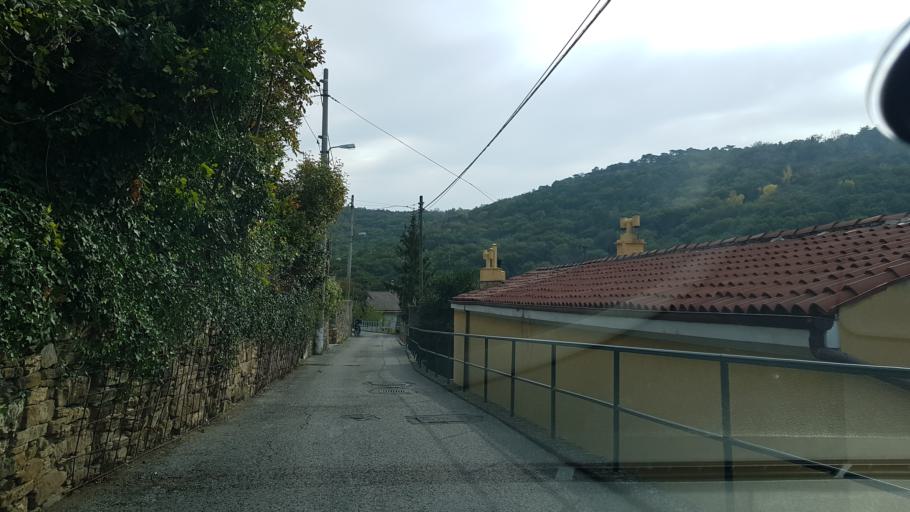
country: IT
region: Friuli Venezia Giulia
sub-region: Provincia di Trieste
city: Trieste
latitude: 45.6506
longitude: 13.8100
